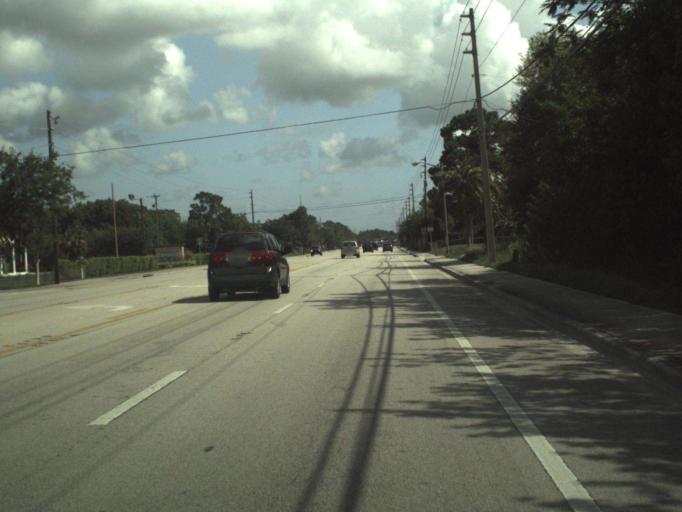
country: US
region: Florida
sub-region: Saint Lucie County
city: Fort Pierce South
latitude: 27.4199
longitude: -80.3501
